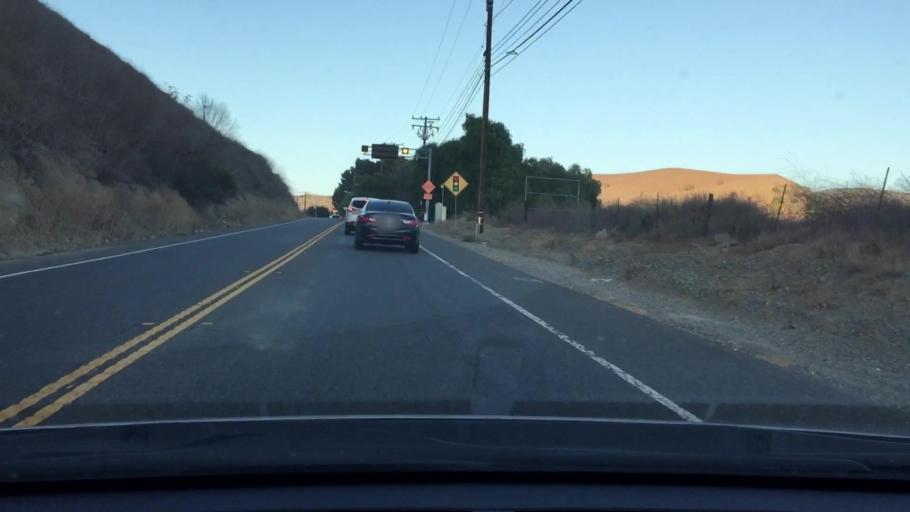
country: US
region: California
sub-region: Orange County
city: Yorba Linda
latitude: 33.9243
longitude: -117.8089
